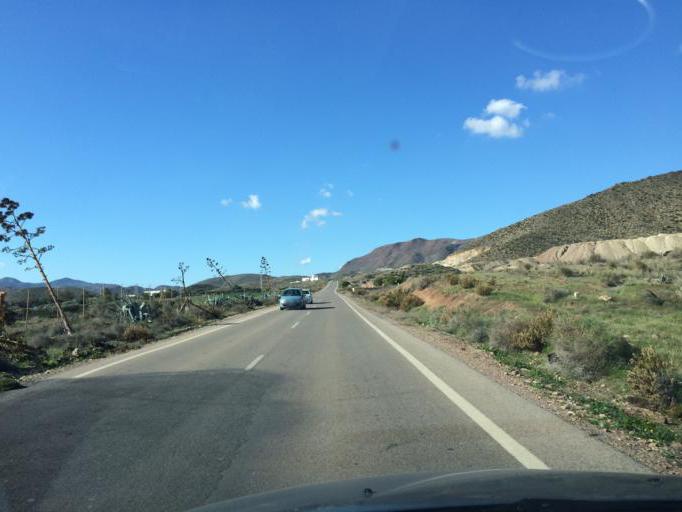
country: ES
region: Andalusia
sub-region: Provincia de Almeria
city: San Jose
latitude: 36.8060
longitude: -2.0693
